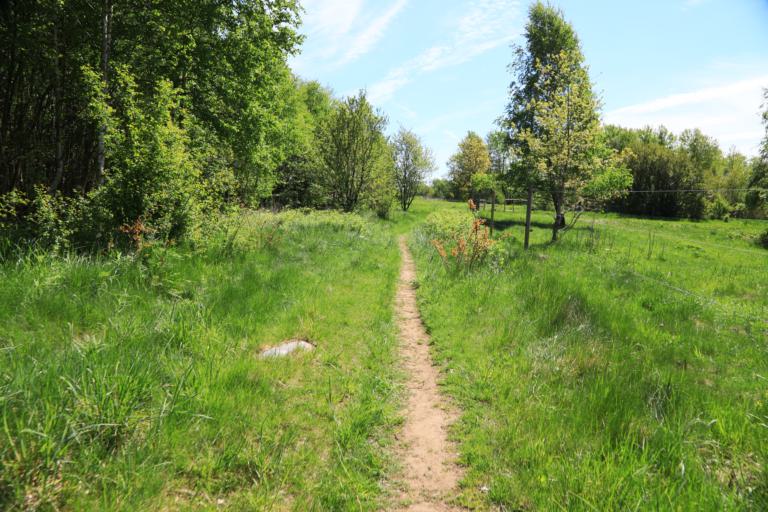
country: SE
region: Halland
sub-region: Varbergs Kommun
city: Varberg
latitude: 57.1156
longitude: 12.3008
